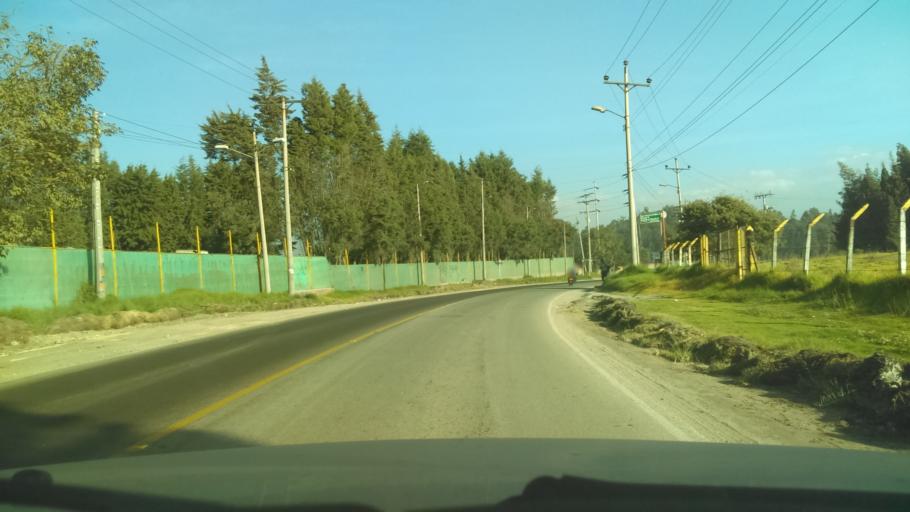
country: CO
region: Cundinamarca
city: Soacha
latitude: 4.5399
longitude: -74.2469
